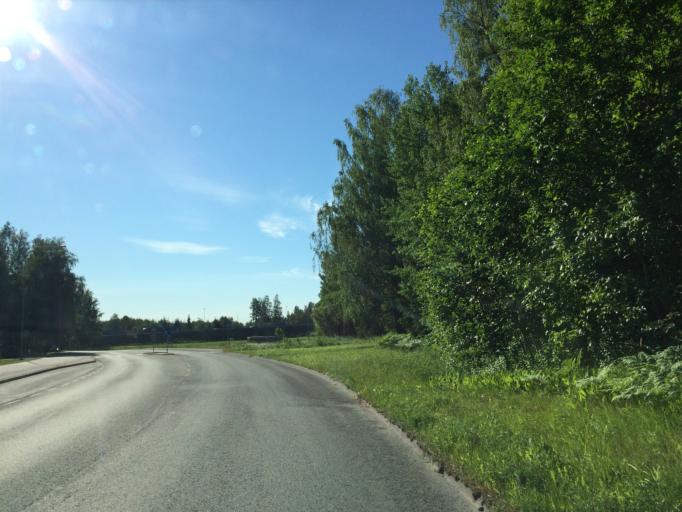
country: FI
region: Haeme
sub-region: Haemeenlinna
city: Haemeenlinna
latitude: 60.9758
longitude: 24.4661
